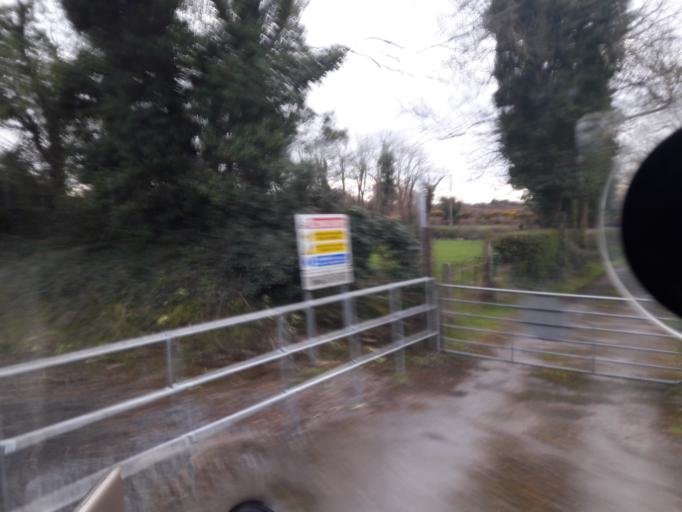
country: IE
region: Leinster
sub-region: An Iarmhi
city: Castlepollard
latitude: 53.6487
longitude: -7.4271
